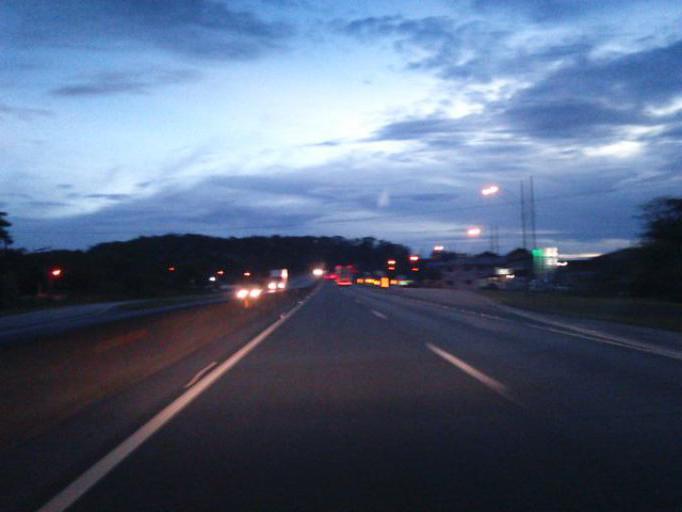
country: BR
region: Santa Catarina
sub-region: Barra Velha
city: Barra Velha
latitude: -26.5472
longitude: -48.7130
